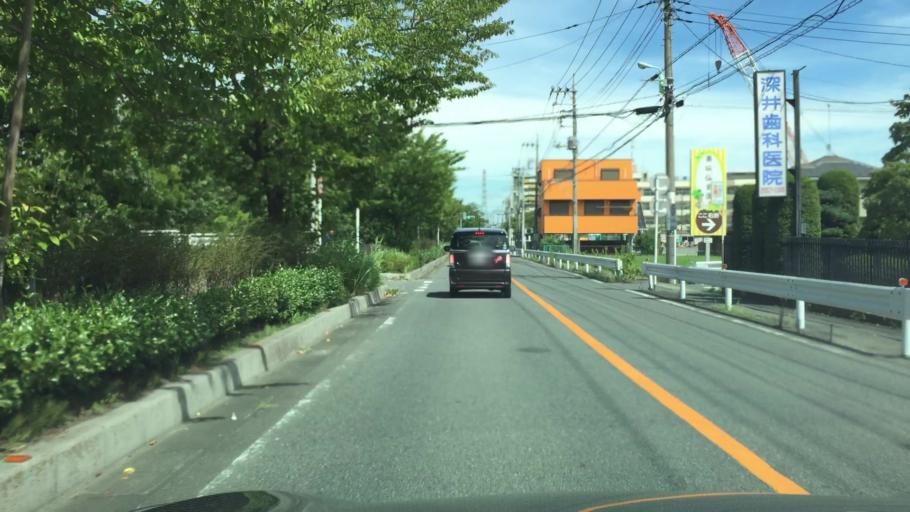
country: JP
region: Saitama
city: Yashio-shi
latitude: 35.8537
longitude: 139.8531
